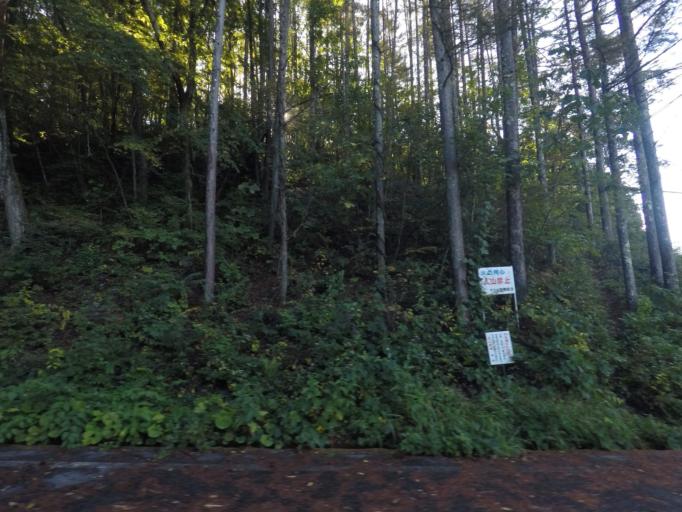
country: JP
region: Nagano
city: Tatsuno
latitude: 35.9635
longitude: 137.7745
